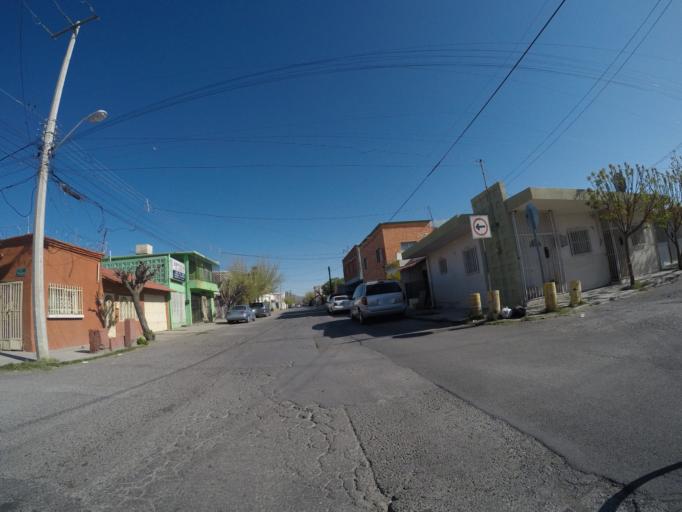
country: MX
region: Chihuahua
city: Ciudad Juarez
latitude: 31.7420
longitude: -106.4719
